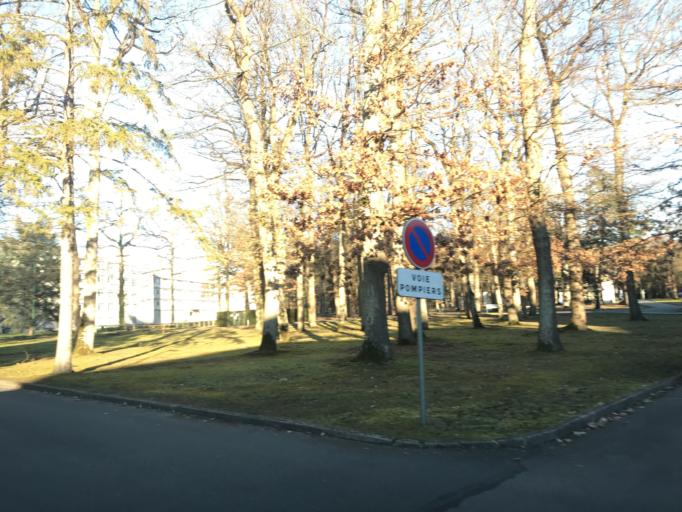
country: FR
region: Haute-Normandie
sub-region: Departement de l'Eure
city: Saint-Sebastien-de-Morsent
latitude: 49.0020
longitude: 1.0771
